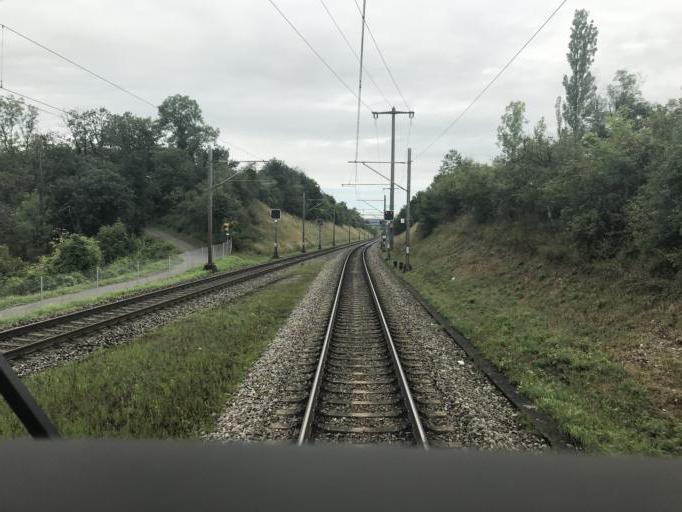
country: CH
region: Zurich
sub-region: Bezirk Buelach
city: Seglingen
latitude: 47.5502
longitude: 8.5239
